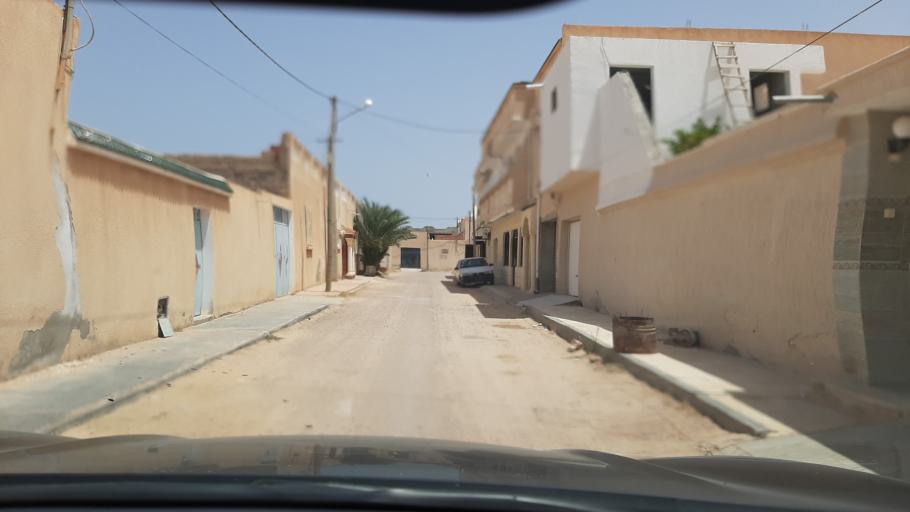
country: TN
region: Qabis
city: Matmata
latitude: 33.6167
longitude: 10.2772
